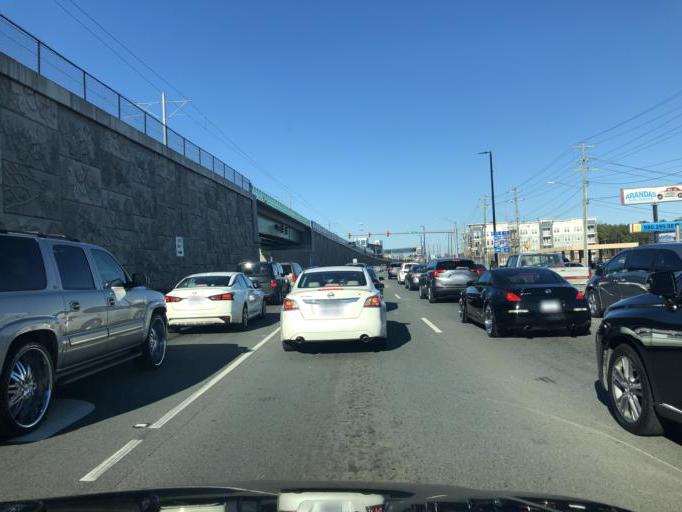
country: US
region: North Carolina
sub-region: Mecklenburg County
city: Charlotte
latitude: 35.2832
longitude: -80.7641
